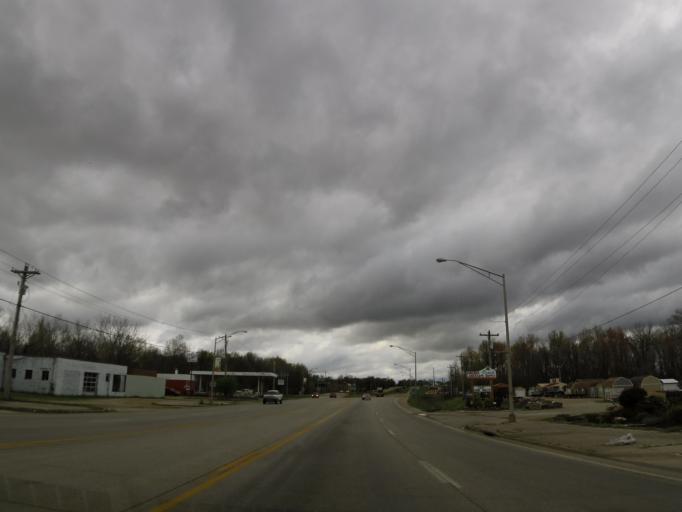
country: US
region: Missouri
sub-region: Butler County
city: Poplar Bluff
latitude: 36.7463
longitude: -90.4118
